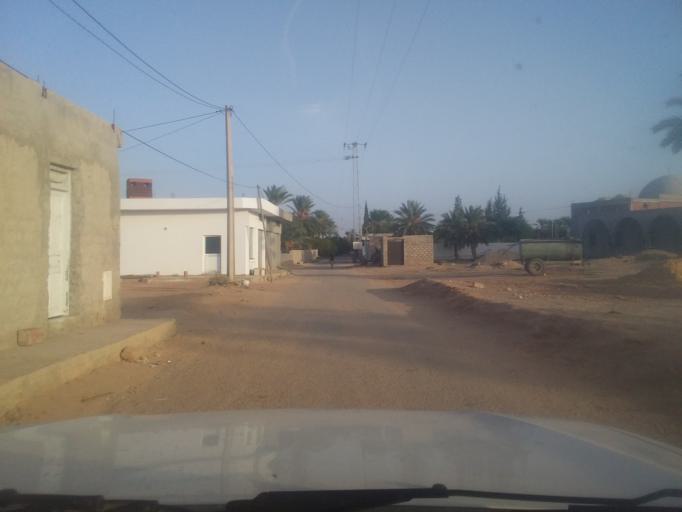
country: TN
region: Qabis
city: Gabes
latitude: 33.6215
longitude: 10.2962
